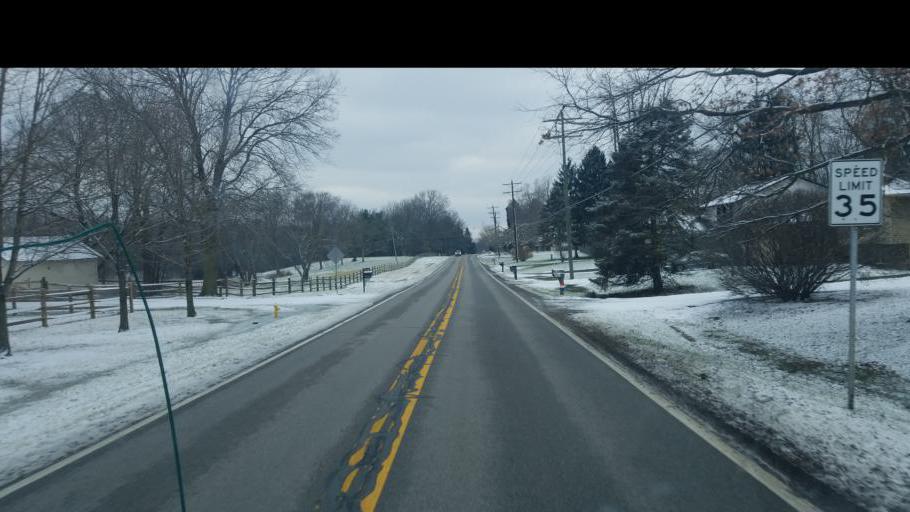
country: US
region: Ohio
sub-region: Franklin County
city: Gahanna
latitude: 40.0283
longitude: -82.8563
